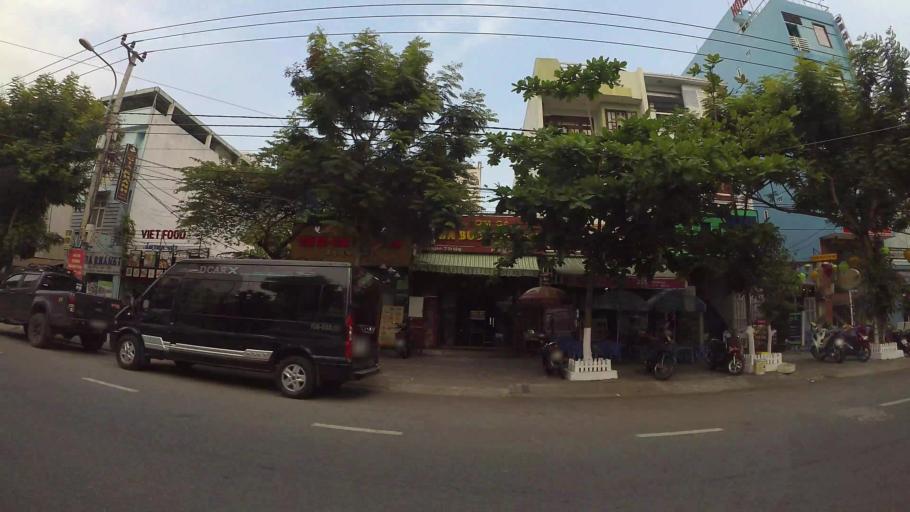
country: VN
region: Da Nang
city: Son Tra
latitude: 16.0663
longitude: 108.2433
